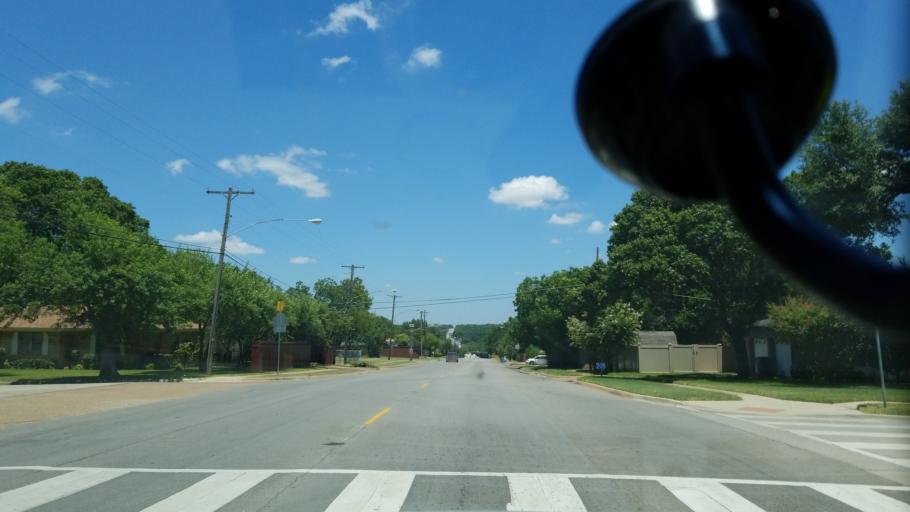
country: US
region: Texas
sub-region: Dallas County
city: Cockrell Hill
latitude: 32.6794
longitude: -96.8147
